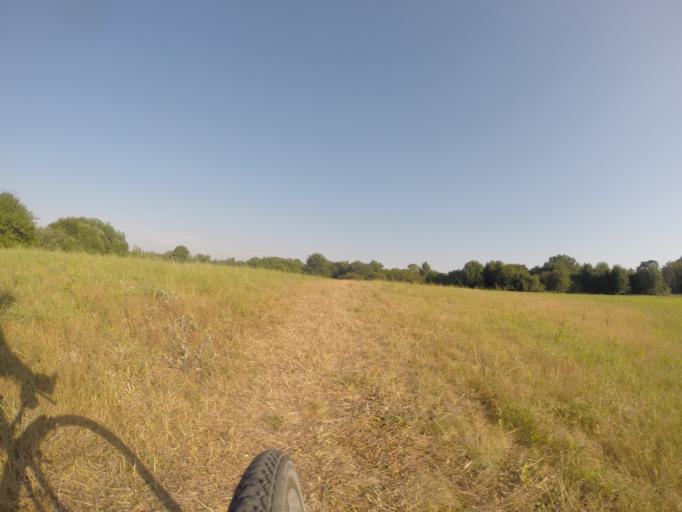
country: DK
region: Capital Region
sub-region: Herlev Kommune
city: Herlev
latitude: 55.7511
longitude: 12.4334
